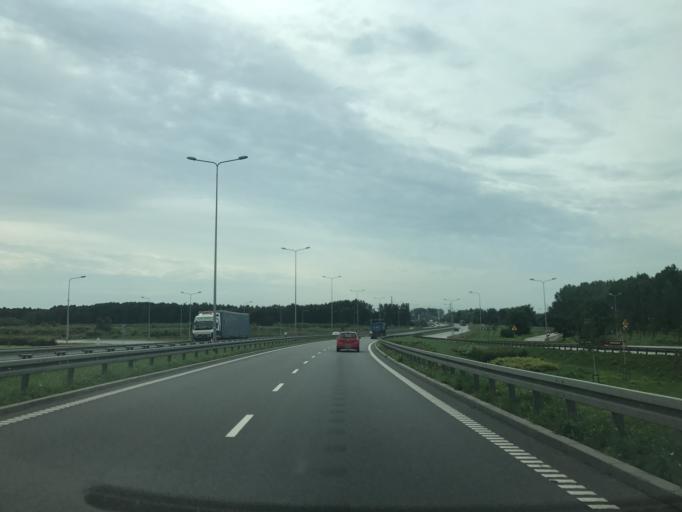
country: PL
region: Pomeranian Voivodeship
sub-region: Gdansk
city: Gdansk
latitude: 54.3762
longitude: 18.6825
